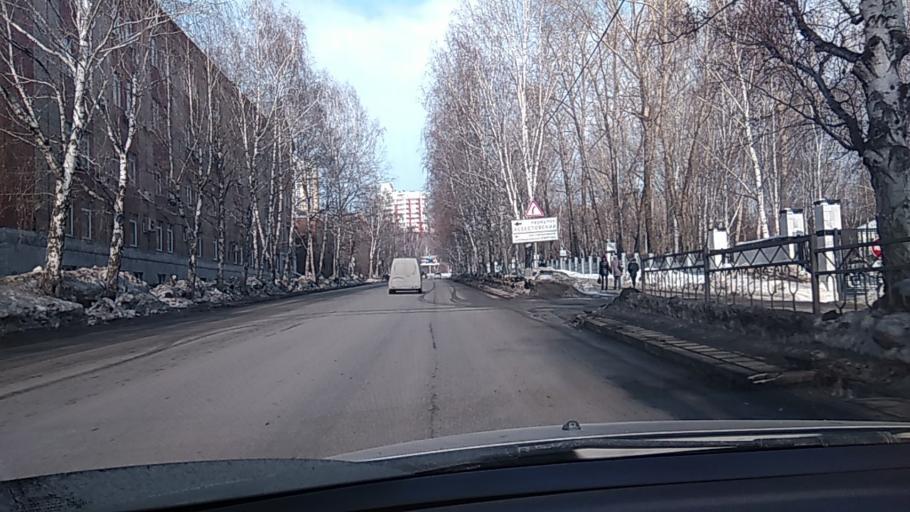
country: RU
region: Sverdlovsk
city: Yekaterinburg
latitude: 56.8470
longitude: 60.6345
